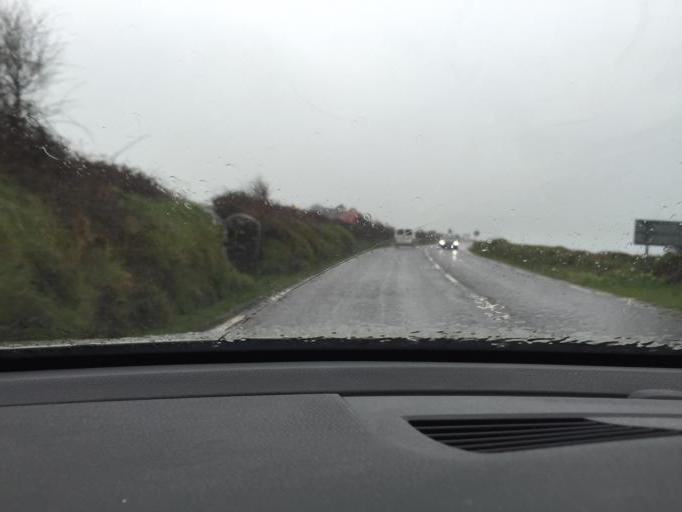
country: IE
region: Munster
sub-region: Ciarrai
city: Dingle
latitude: 52.1351
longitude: -10.2654
